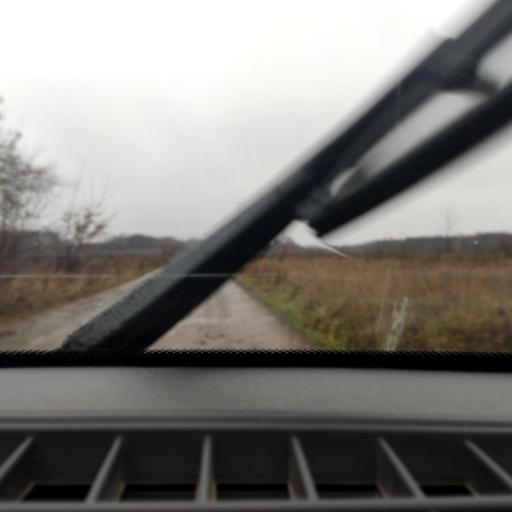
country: RU
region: Bashkortostan
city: Avdon
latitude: 54.6362
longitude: 55.7258
